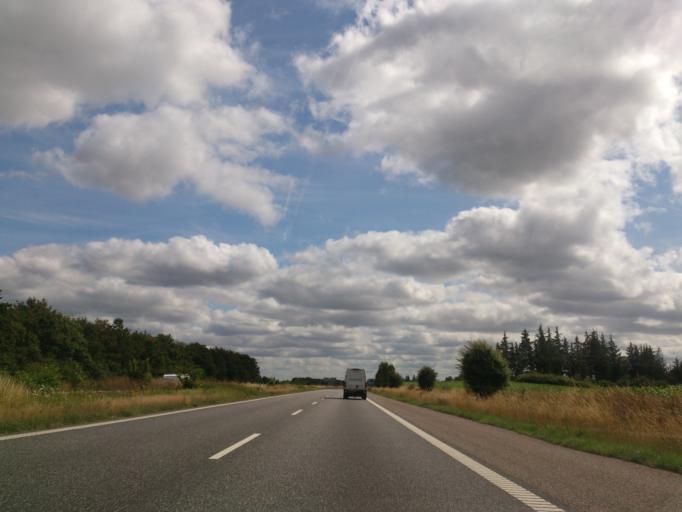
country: DK
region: South Denmark
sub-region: Aabenraa Kommune
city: Krusa
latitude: 54.9275
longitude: 9.3834
